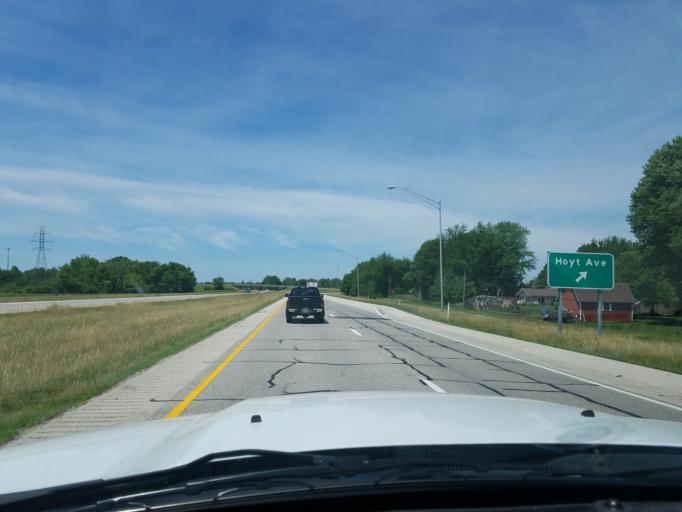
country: US
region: Indiana
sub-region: Delaware County
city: Muncie
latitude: 40.1424
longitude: -85.4248
